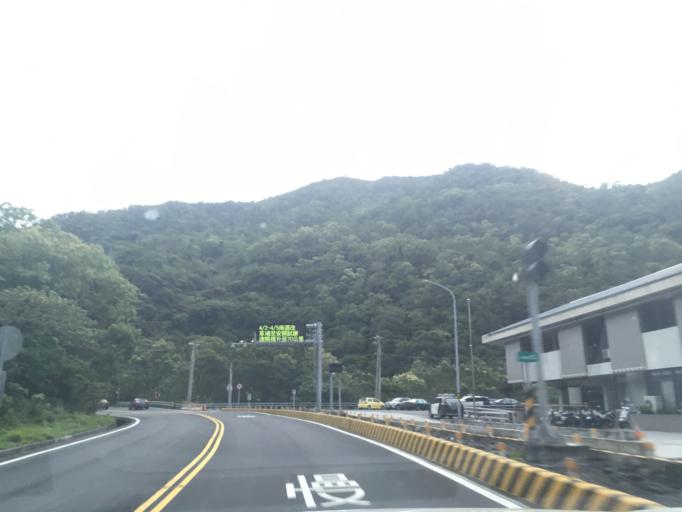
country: TW
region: Taiwan
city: Hengchun
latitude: 22.2314
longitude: 120.8006
